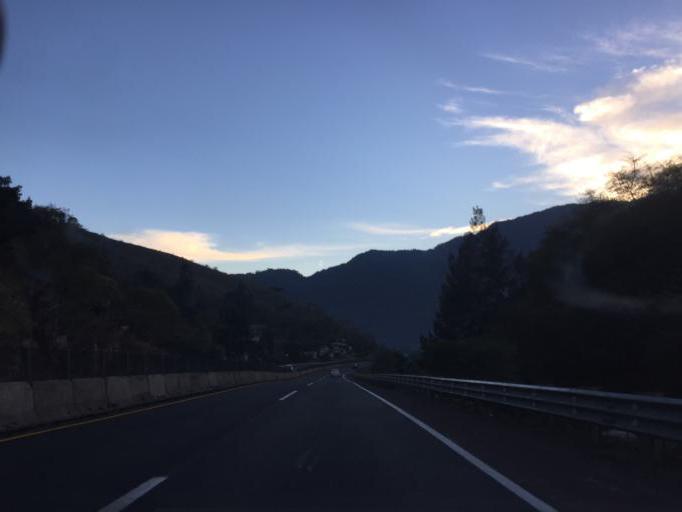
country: MX
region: Veracruz
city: Ciudad Mendoza
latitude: 18.8178
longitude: -97.1715
